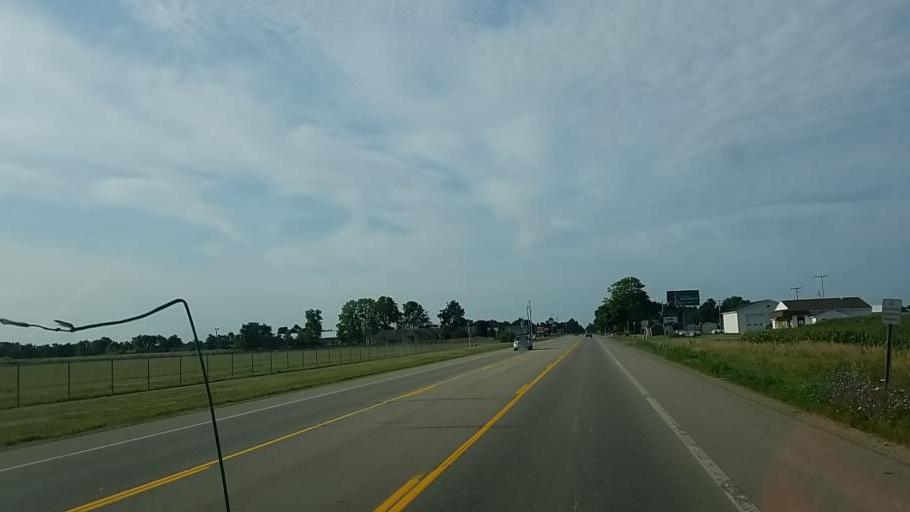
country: US
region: Michigan
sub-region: Ionia County
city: Ionia
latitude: 42.9386
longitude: -85.0748
